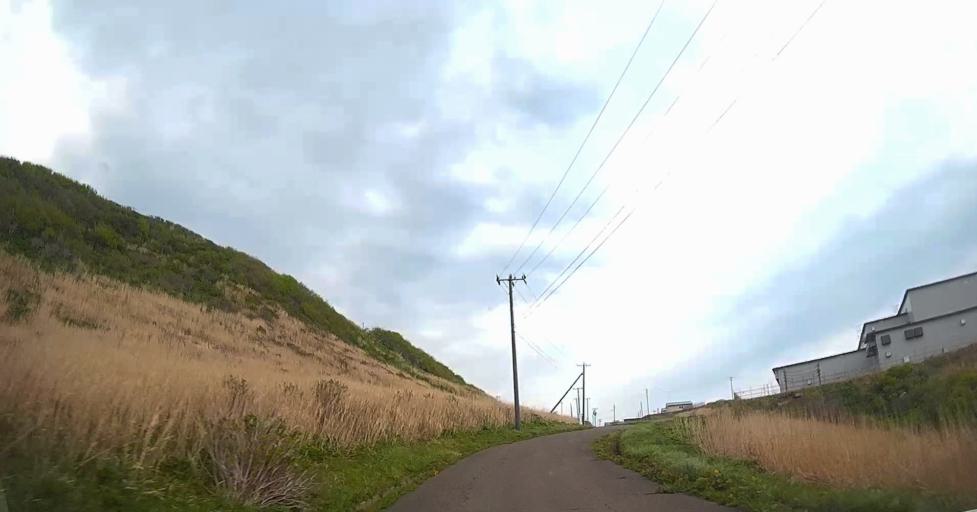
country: JP
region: Aomori
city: Shimokizukuri
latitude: 41.2548
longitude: 140.3431
